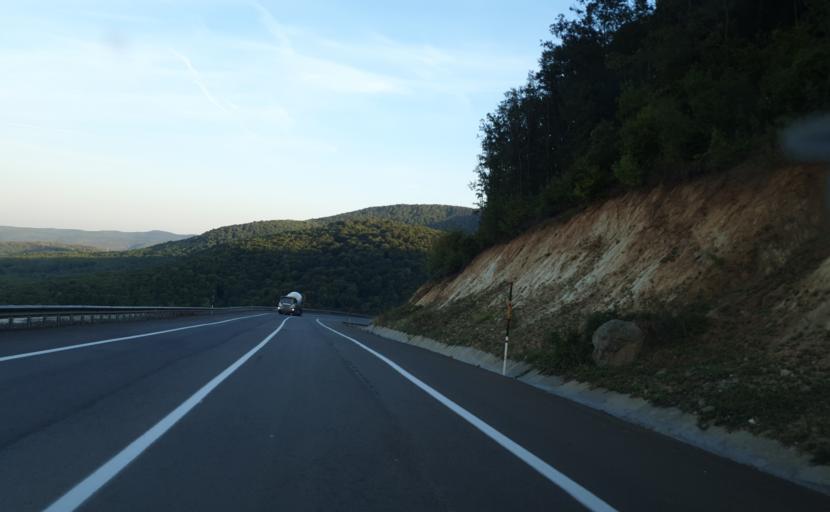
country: TR
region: Kirklareli
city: Sergen
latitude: 41.8139
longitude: 27.7464
